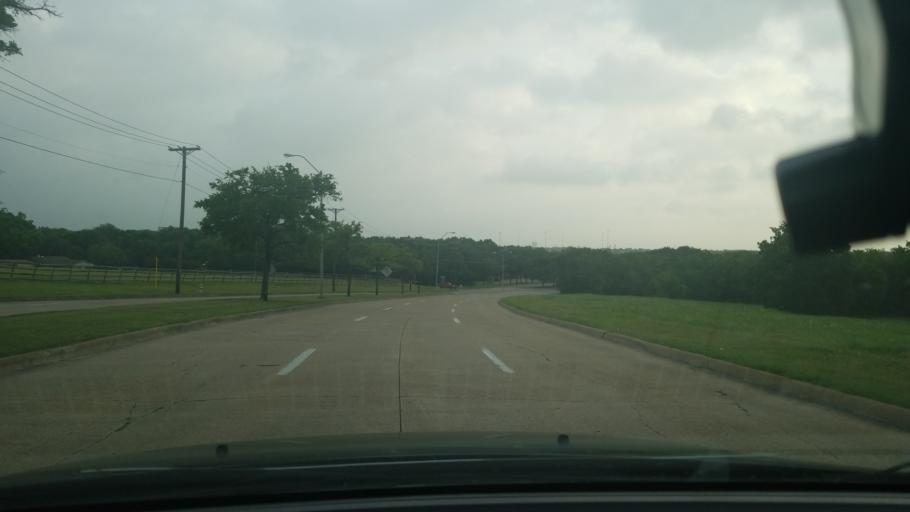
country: US
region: Texas
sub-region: Dallas County
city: Mesquite
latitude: 32.7794
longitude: -96.6299
